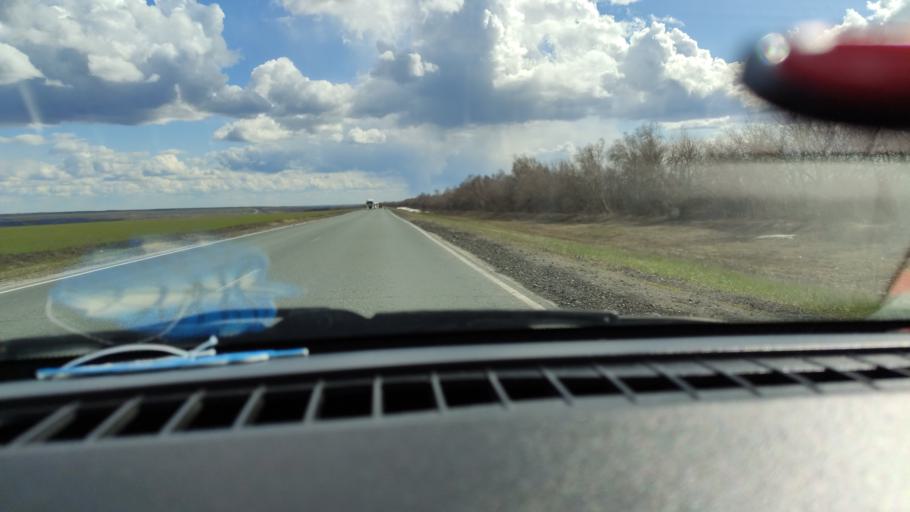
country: RU
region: Saratov
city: Dukhovnitskoye
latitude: 52.7705
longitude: 48.2362
